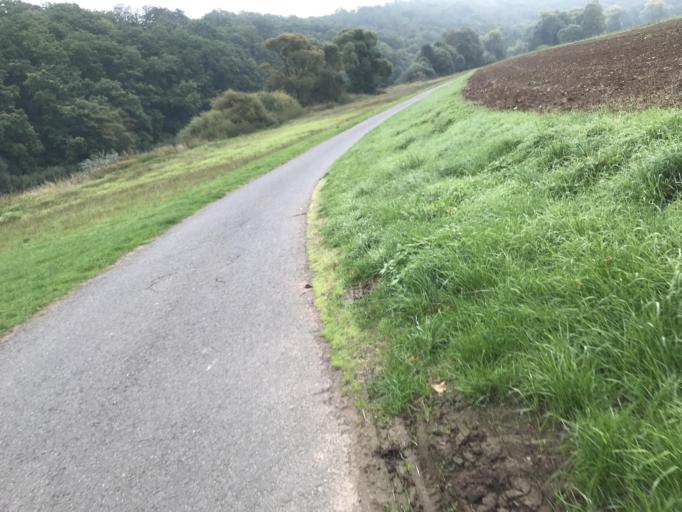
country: DE
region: Hesse
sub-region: Regierungsbezirk Kassel
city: Fuldabruck
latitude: 51.2342
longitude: 9.4714
